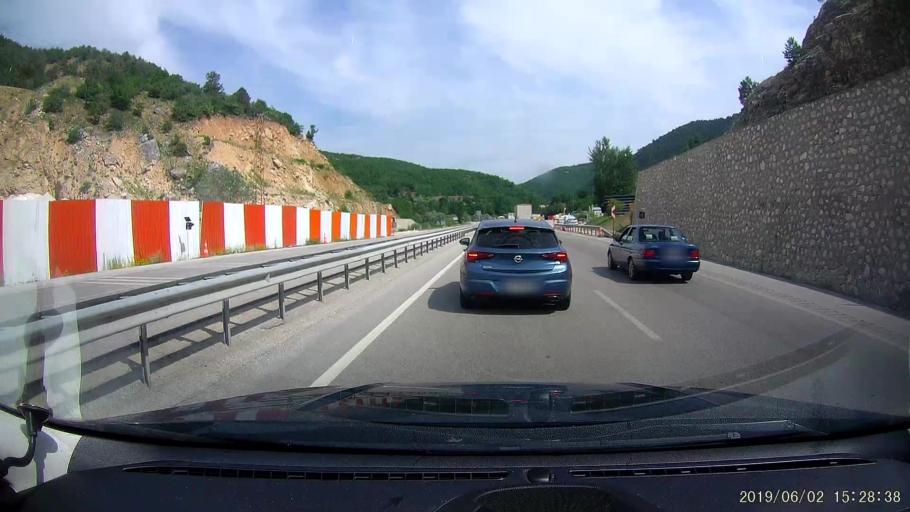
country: TR
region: Amasya
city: Saraycik
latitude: 40.9759
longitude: 35.0799
